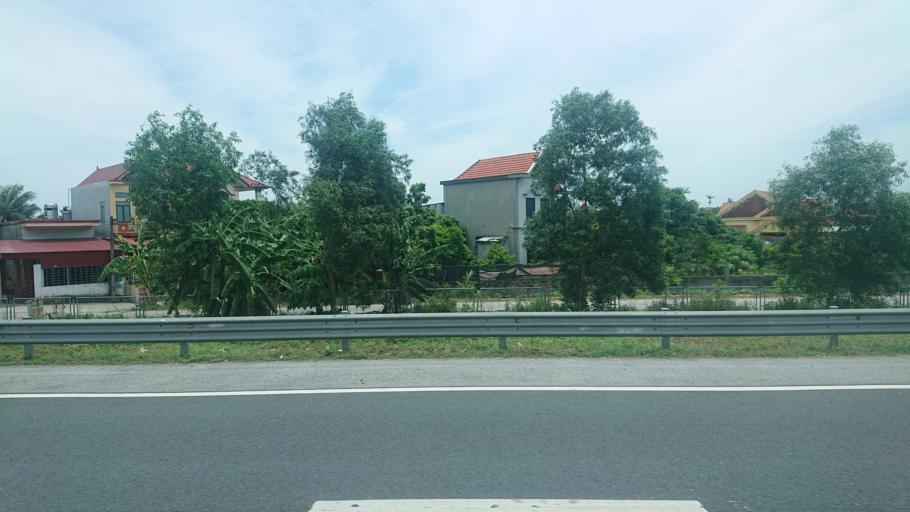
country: VN
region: Hai Phong
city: An Lao
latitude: 20.8036
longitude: 106.5239
